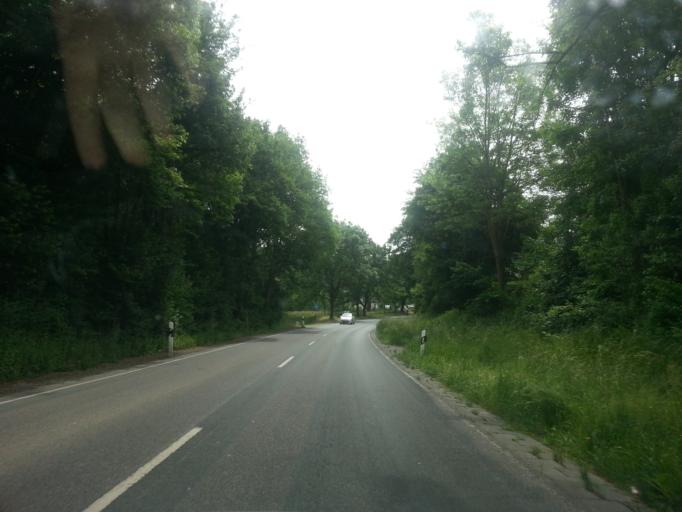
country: DE
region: Hesse
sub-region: Regierungsbezirk Darmstadt
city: Seeheim-Jugenheim
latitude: 49.7403
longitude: 8.6547
